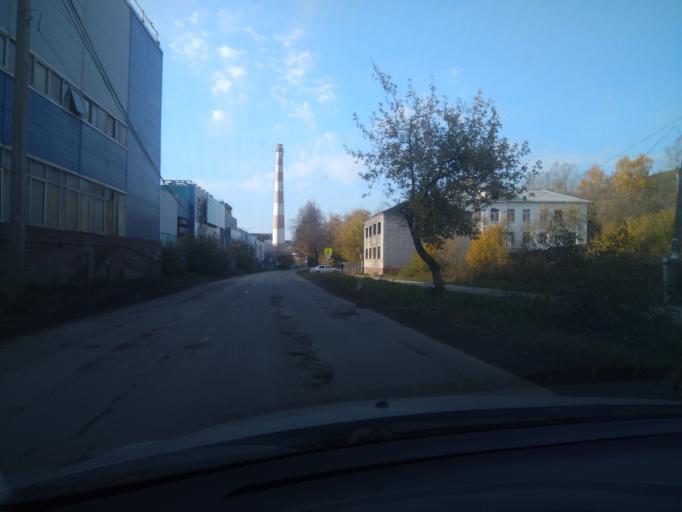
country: RU
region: Sverdlovsk
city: Nizhniye Sergi
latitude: 56.6661
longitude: 59.3130
